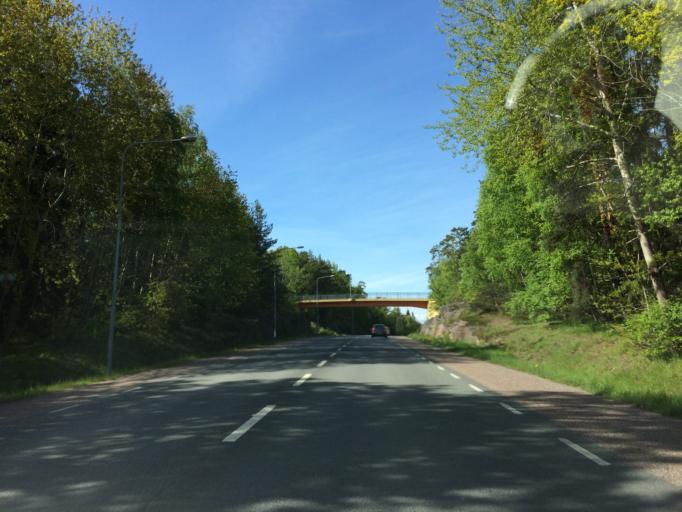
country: SE
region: Stockholm
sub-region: Sollentuna Kommun
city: Sollentuna
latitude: 59.4284
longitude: 17.9959
